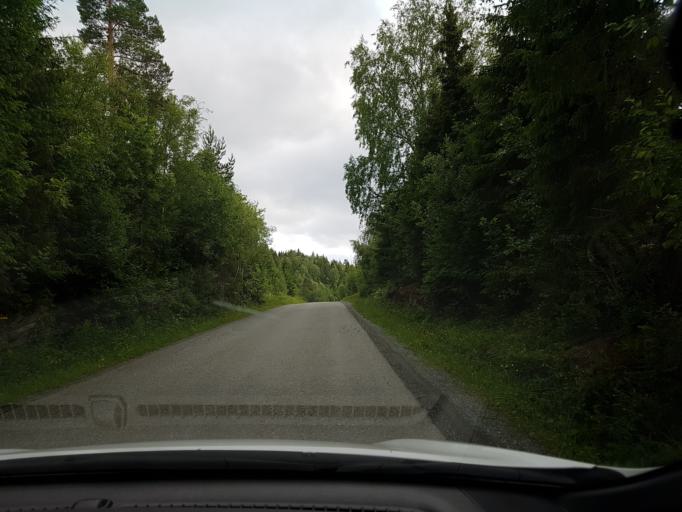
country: NO
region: Nord-Trondelag
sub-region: Frosta
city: Frosta
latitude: 63.6210
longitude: 10.7608
